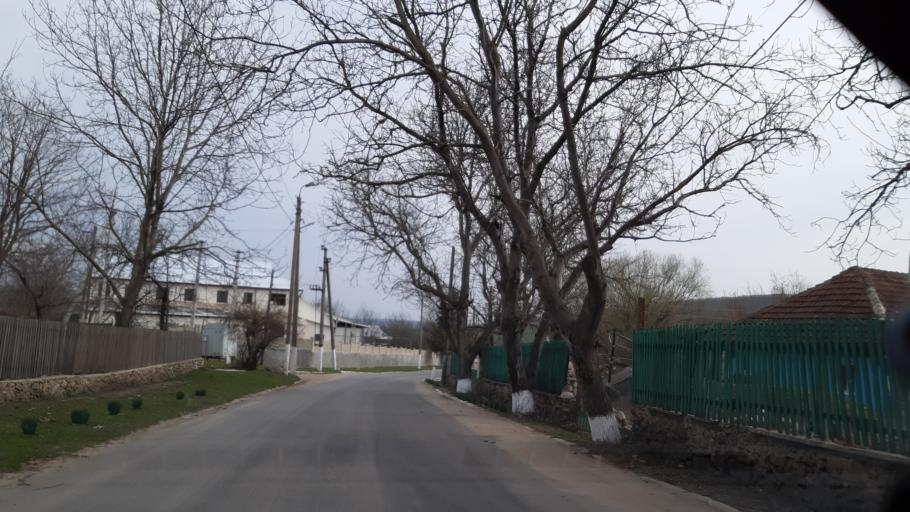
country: MD
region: Soldanesti
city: Soldanesti
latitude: 47.6828
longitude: 28.7808
